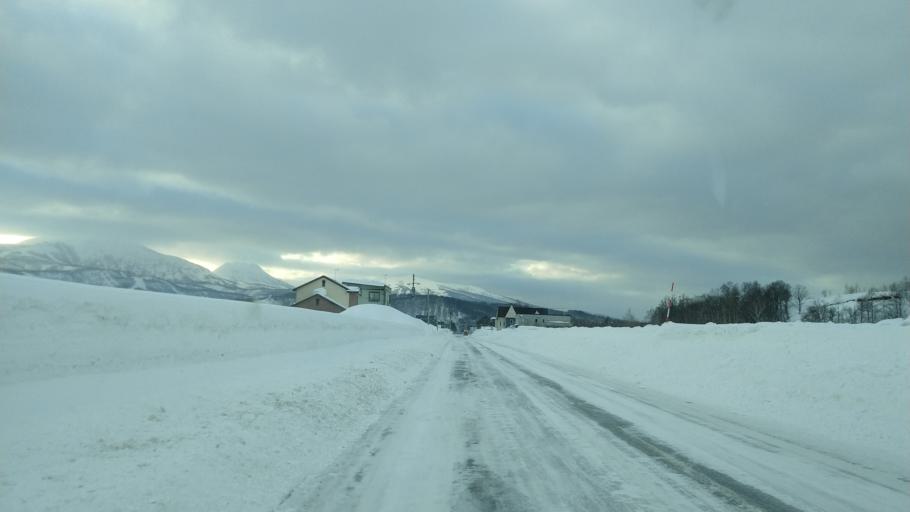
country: JP
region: Hokkaido
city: Niseko Town
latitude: 42.9084
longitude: 140.7657
